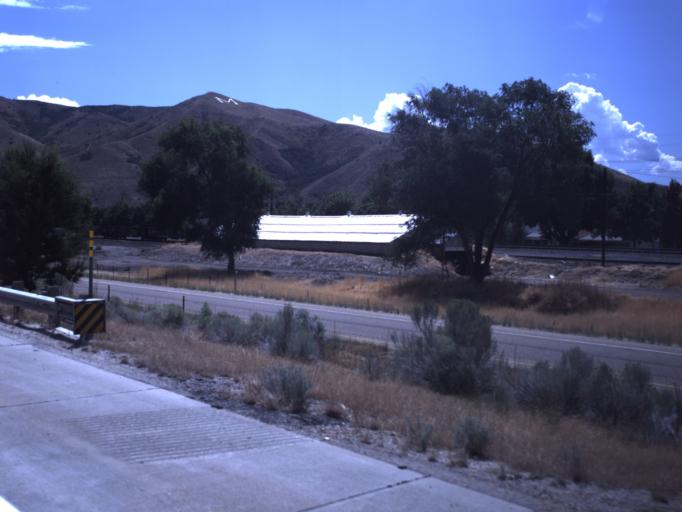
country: US
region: Utah
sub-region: Morgan County
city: Morgan
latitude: 41.0443
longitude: -111.6697
